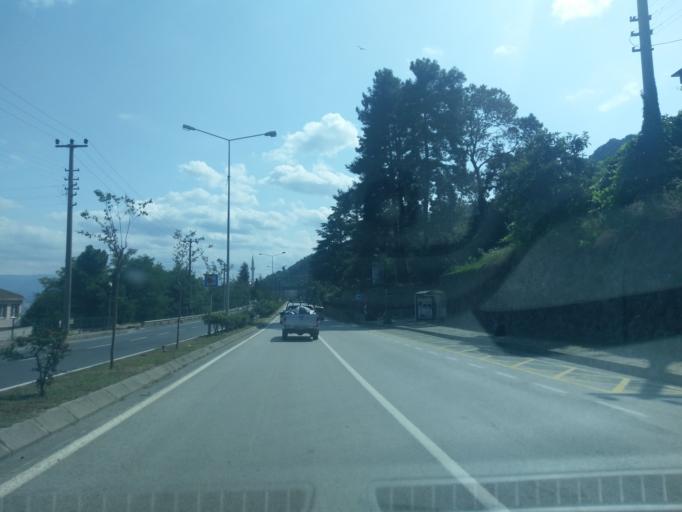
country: TR
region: Ordu
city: Ordu
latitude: 41.0063
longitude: 37.8695
